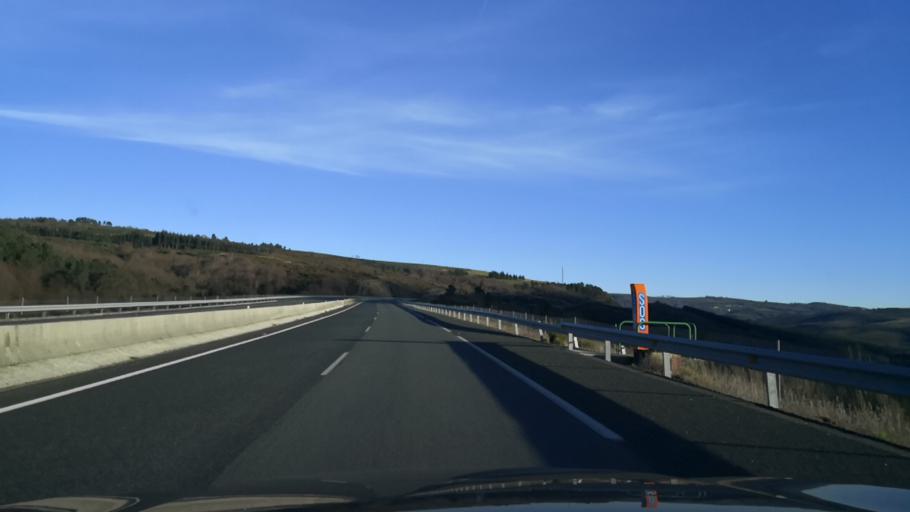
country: ES
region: Galicia
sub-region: Provincia de Pontevedra
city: Lalin
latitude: 42.6015
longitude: -8.0955
